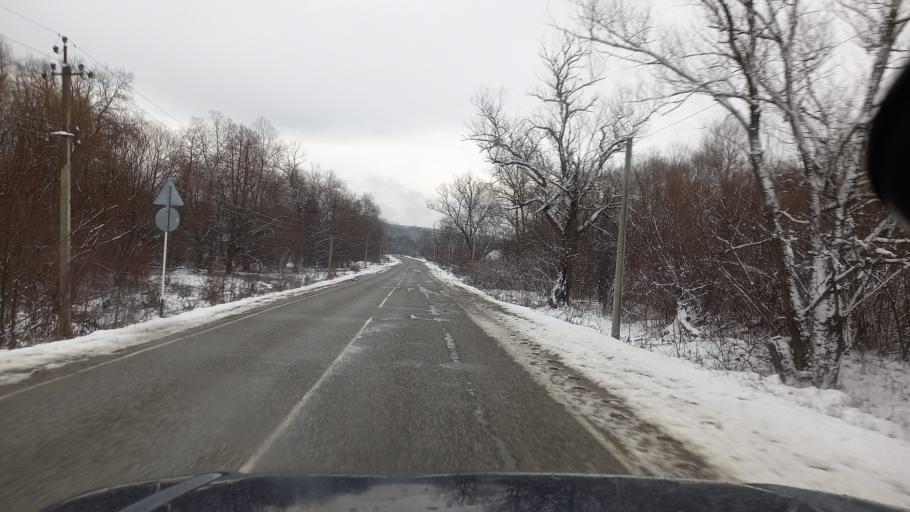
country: RU
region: Adygeya
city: Abadzekhskaya
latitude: 44.3595
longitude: 40.2872
